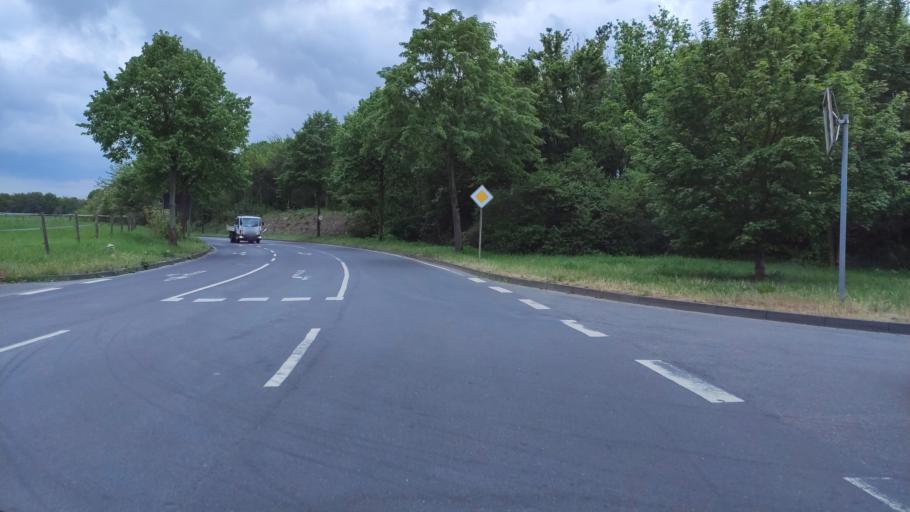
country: DE
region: North Rhine-Westphalia
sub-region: Regierungsbezirk Dusseldorf
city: Kaarst
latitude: 51.2011
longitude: 6.6169
